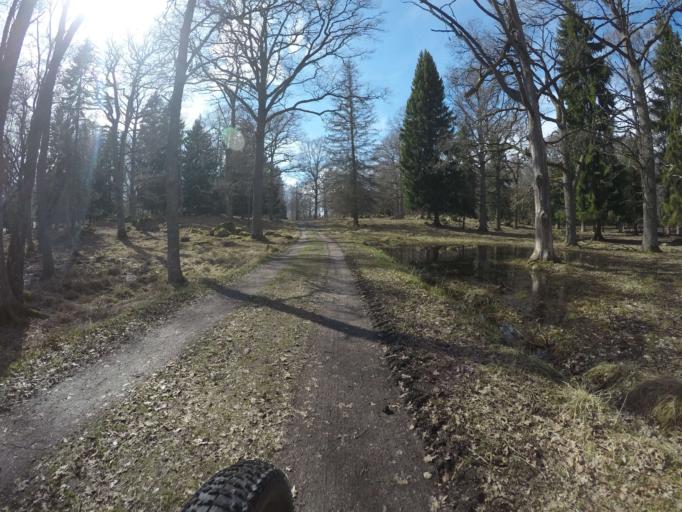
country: SE
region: Vaestmanland
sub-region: Kungsors Kommun
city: Kungsoer
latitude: 59.2733
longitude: 16.1380
